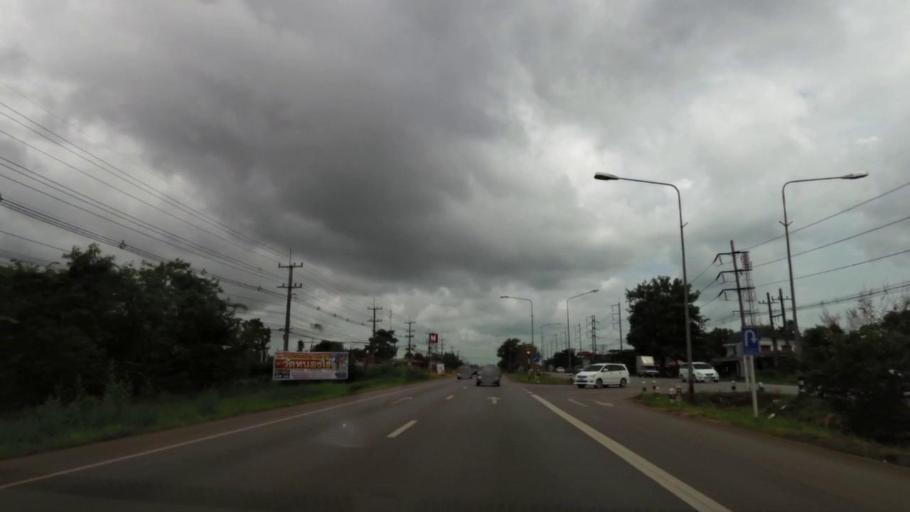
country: TH
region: Chanthaburi
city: Na Yai Am
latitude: 12.7767
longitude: 101.8311
